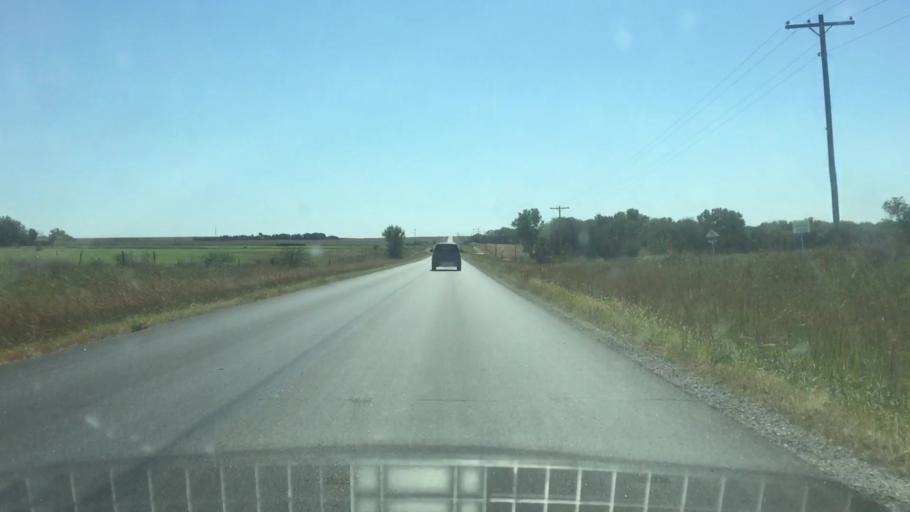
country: US
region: Kansas
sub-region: Marshall County
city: Marysville
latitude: 39.8839
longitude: -96.6010
